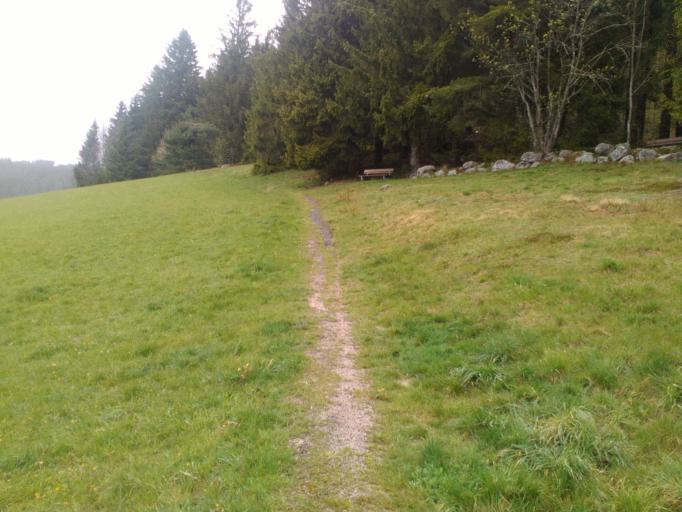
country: DE
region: Baden-Wuerttemberg
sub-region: Freiburg Region
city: Schluchsee
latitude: 47.8230
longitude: 8.1788
